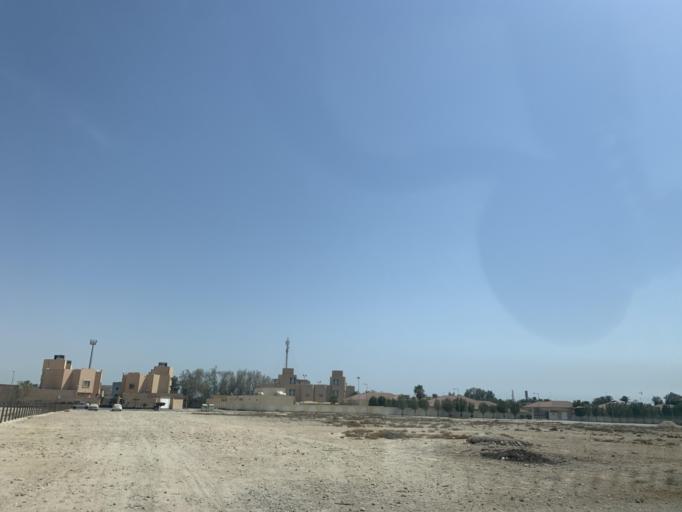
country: BH
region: Central Governorate
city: Madinat Hamad
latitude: 26.1804
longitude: 50.4729
